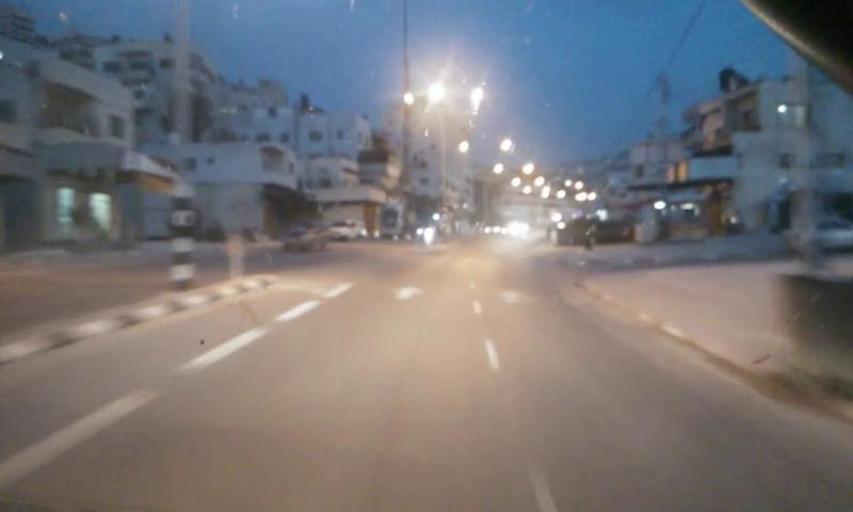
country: PS
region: West Bank
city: Zawata
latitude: 32.2393
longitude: 35.2321
